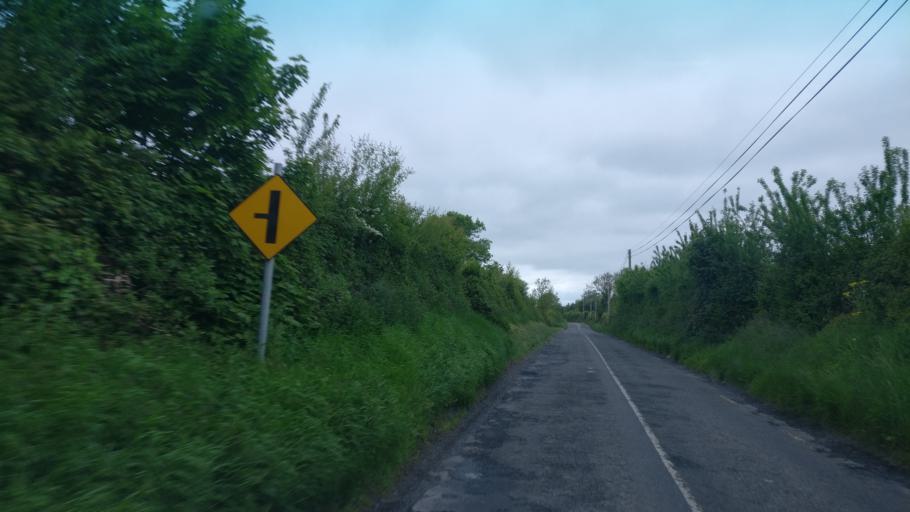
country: IE
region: Connaught
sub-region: County Galway
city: Portumna
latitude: 53.1037
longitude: -8.2563
